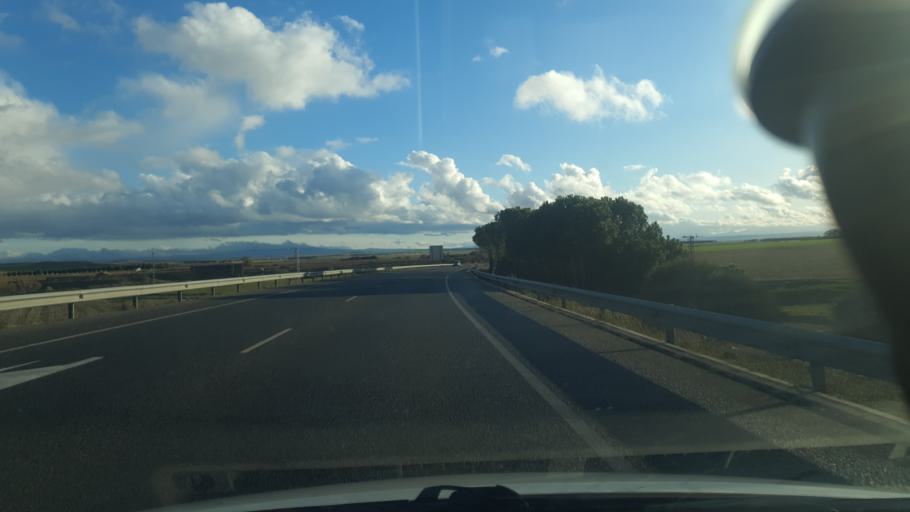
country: ES
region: Castille and Leon
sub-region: Provincia de Segovia
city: Codorniz
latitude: 41.0470
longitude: -4.6225
